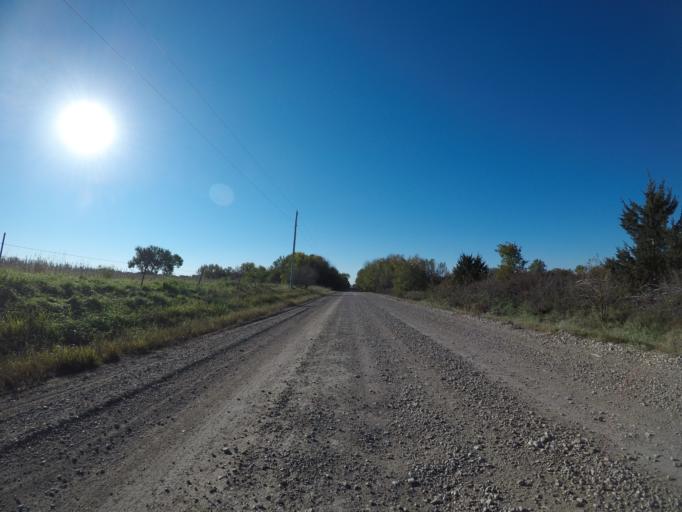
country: US
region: Kansas
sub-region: Morris County
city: Council Grove
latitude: 38.8520
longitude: -96.4829
